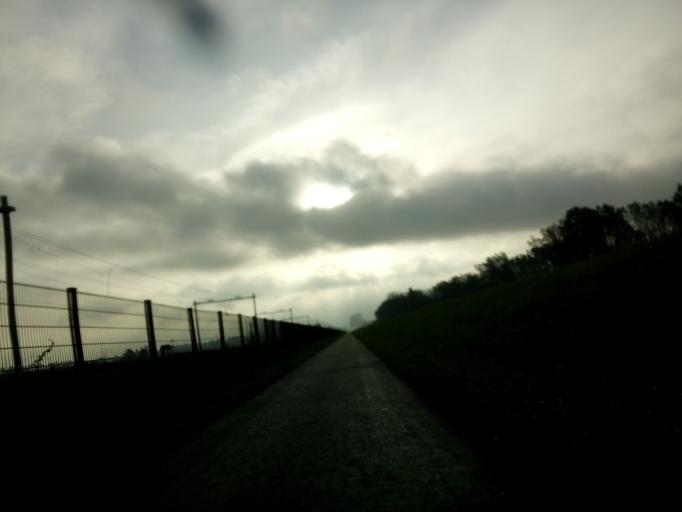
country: NL
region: South Holland
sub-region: Gemeente Westland
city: Maasdijk
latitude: 51.9439
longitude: 4.1958
